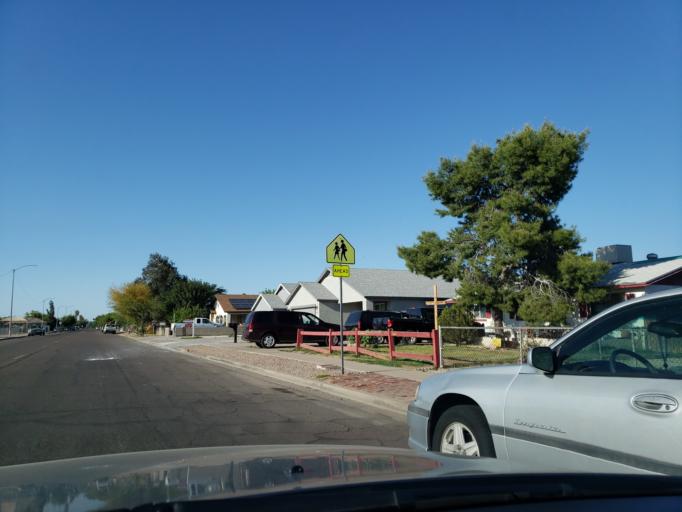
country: US
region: Arizona
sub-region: Maricopa County
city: Glendale
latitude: 33.5333
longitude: -112.1774
